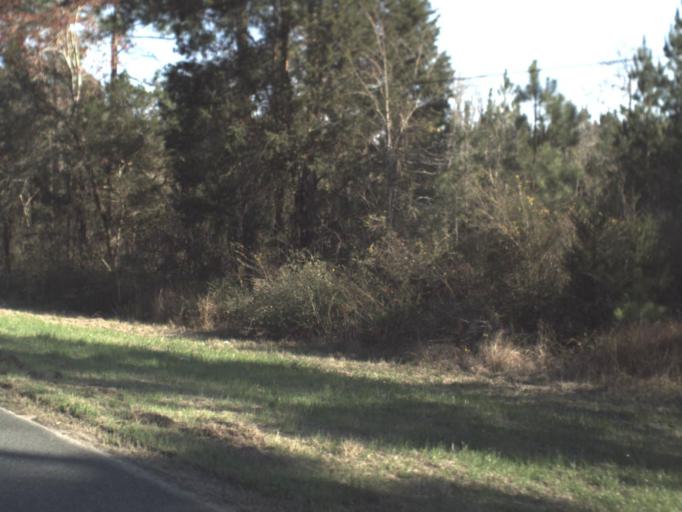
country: US
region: Florida
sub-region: Jackson County
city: Marianna
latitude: 30.7450
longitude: -85.1643
